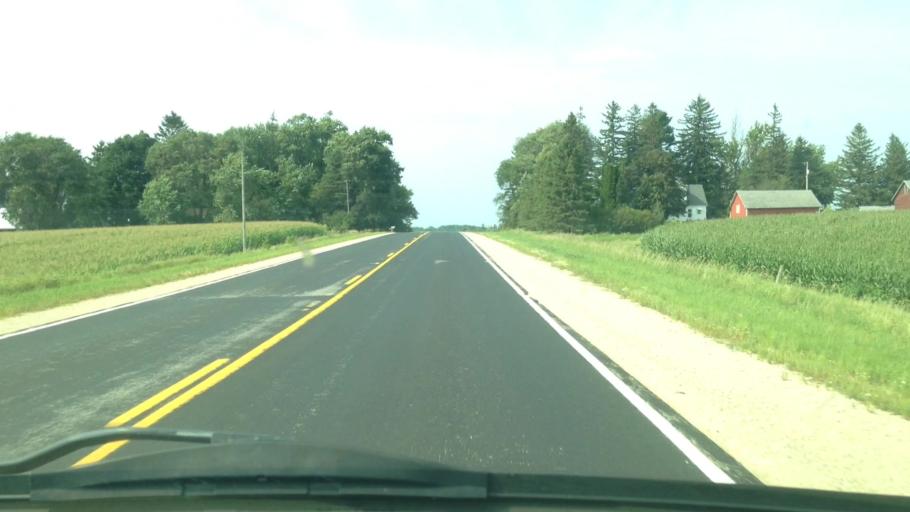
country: US
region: Minnesota
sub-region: Winona County
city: Lewiston
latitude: 43.9067
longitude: -91.9594
